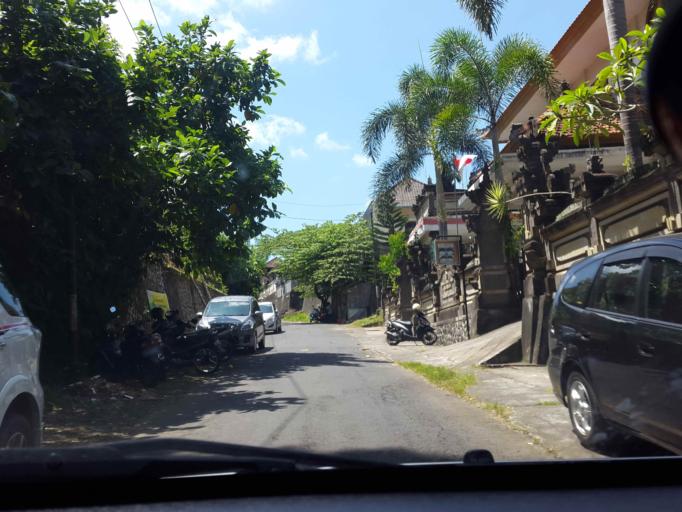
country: ID
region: Bali
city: Banjar Wangsian
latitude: -8.4987
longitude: 115.4017
